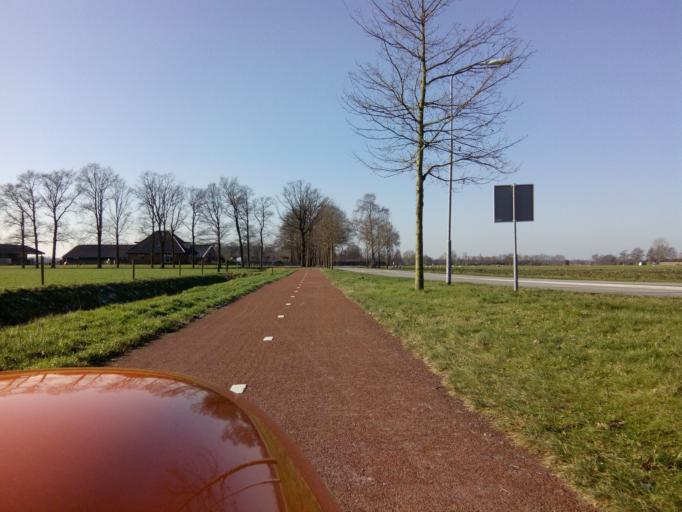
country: NL
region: Gelderland
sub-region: Gemeente Barneveld
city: Terschuur
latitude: 52.1197
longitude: 5.5342
